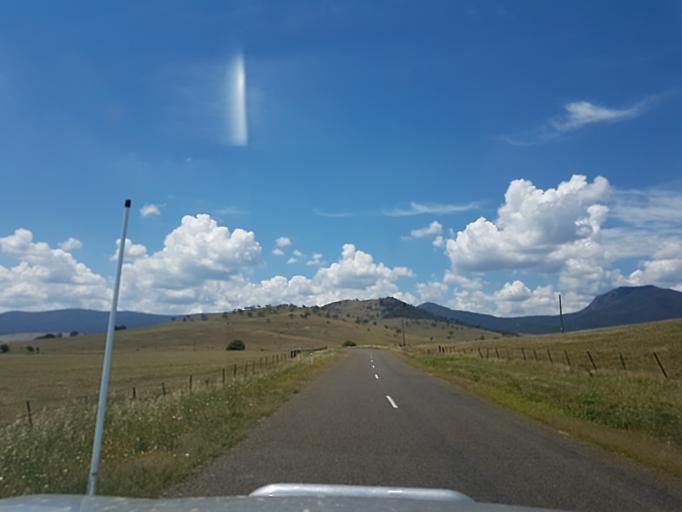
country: AU
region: Victoria
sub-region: Alpine
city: Mount Beauty
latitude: -36.9576
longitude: 147.7600
